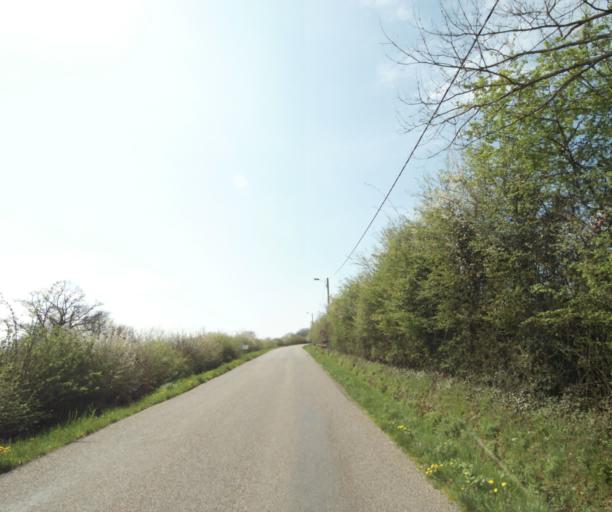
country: FR
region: Bourgogne
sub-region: Departement de Saone-et-Loire
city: Palinges
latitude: 46.5538
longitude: 4.2018
